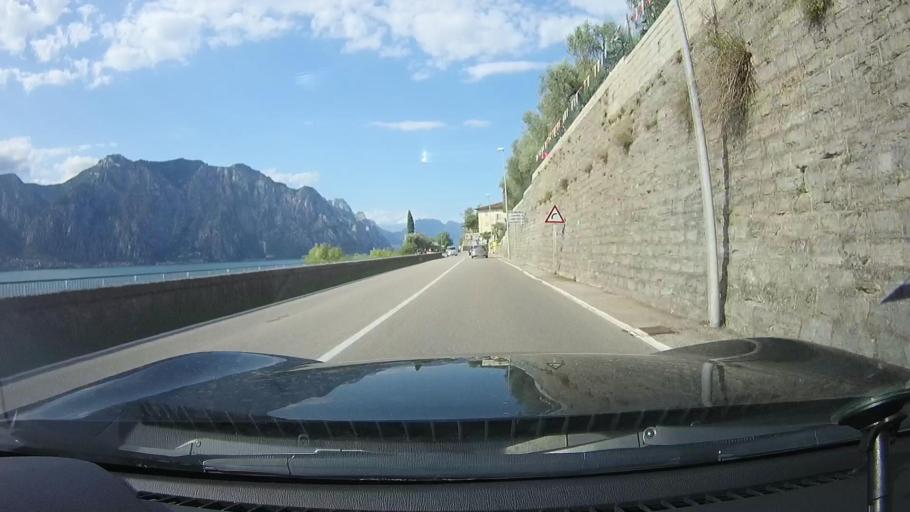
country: IT
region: Veneto
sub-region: Provincia di Verona
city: Malcesine
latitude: 45.7828
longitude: 10.8184
